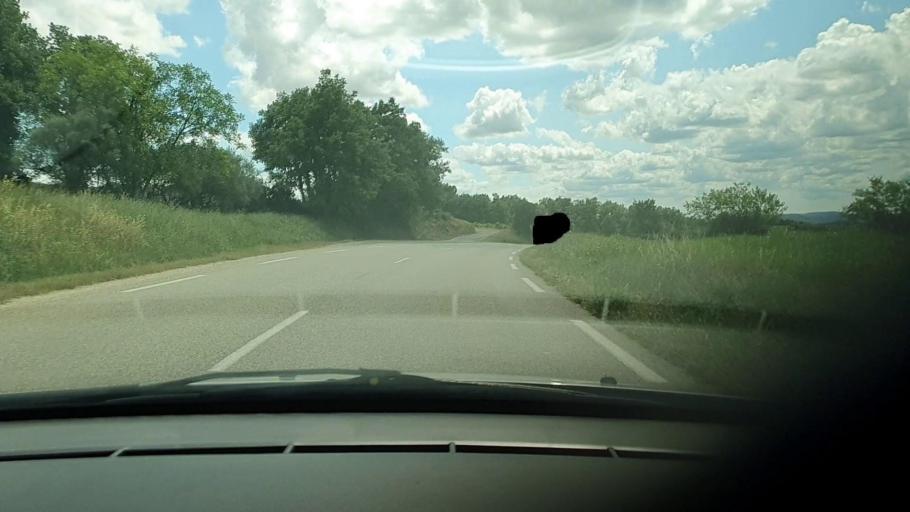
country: FR
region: Languedoc-Roussillon
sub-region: Departement du Gard
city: Moussac
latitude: 44.0230
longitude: 4.2342
